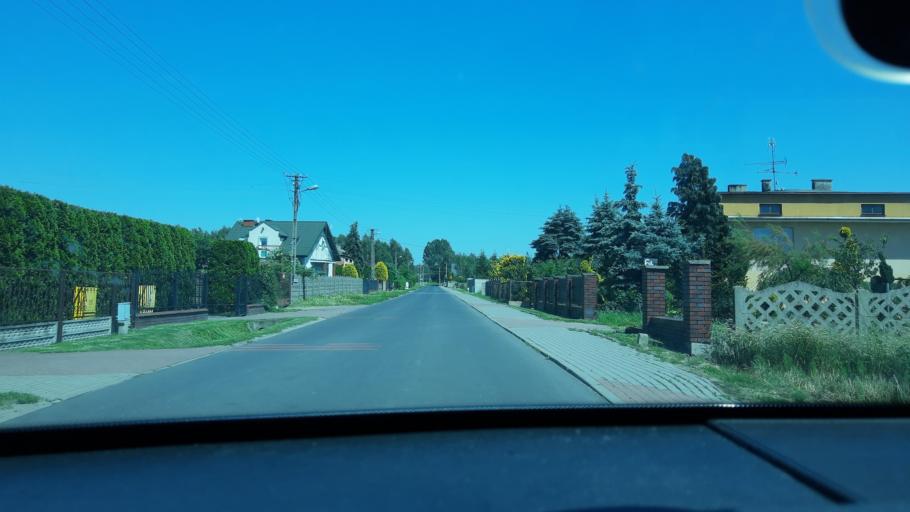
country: PL
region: Lodz Voivodeship
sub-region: Powiat zdunskowolski
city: Zdunska Wola
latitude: 51.6213
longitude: 18.9579
